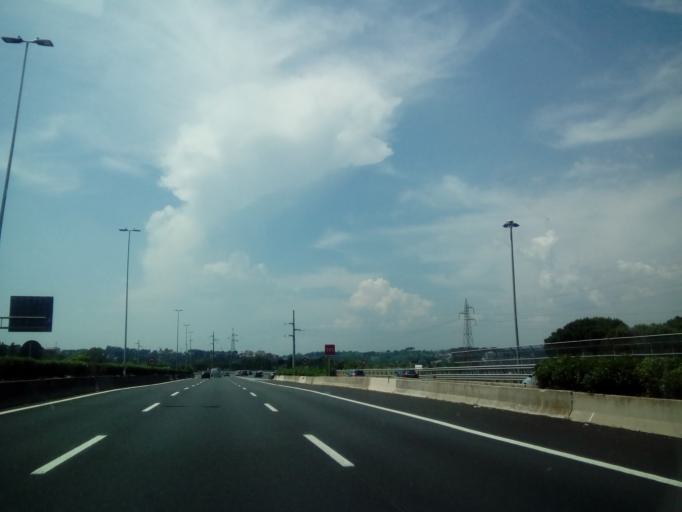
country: IT
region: Latium
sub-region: Citta metropolitana di Roma Capitale
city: Monte Caminetto
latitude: 41.9893
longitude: 12.5127
